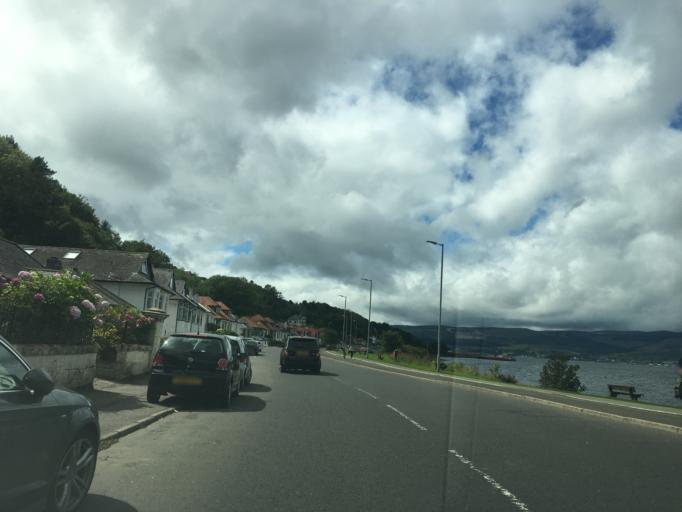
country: GB
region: Scotland
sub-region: Inverclyde
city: Gourock
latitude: 55.9540
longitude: -4.8380
